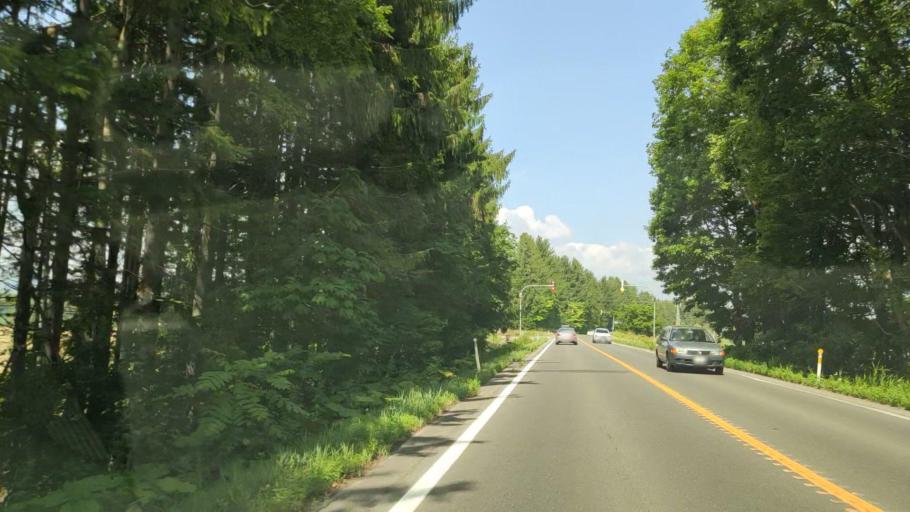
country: JP
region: Hokkaido
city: Shimo-furano
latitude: 43.5111
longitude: 142.4514
